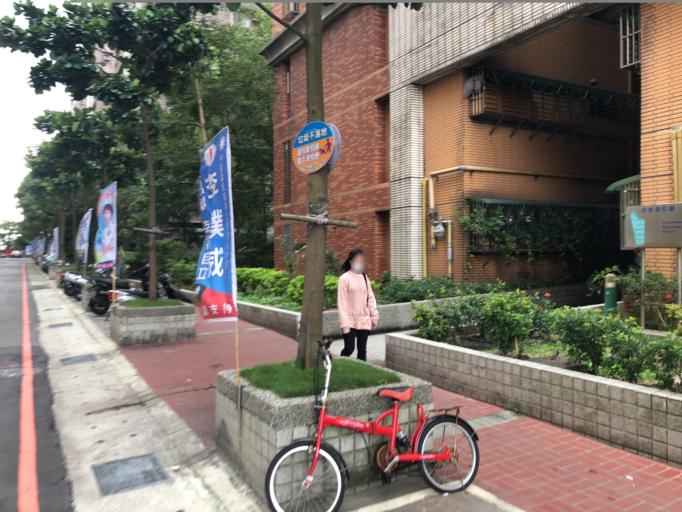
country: TW
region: Taiwan
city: Taoyuan City
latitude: 24.9669
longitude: 121.2518
